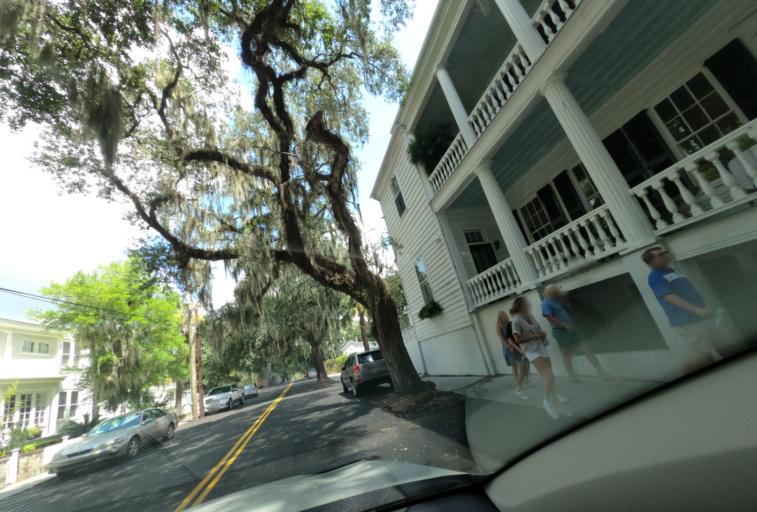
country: US
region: South Carolina
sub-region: Beaufort County
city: Beaufort
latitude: 32.4328
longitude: -80.6740
